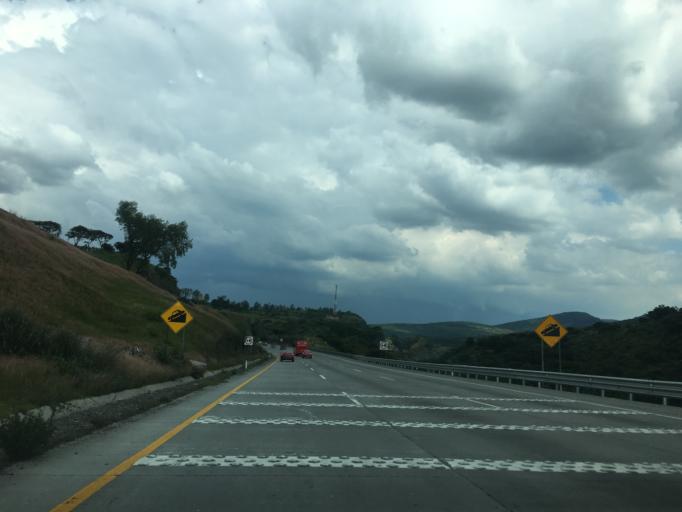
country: MX
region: Hidalgo
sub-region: Tepeji del Rio de Ocampo
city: Santiago Tlautla
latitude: 19.9715
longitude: -99.4335
